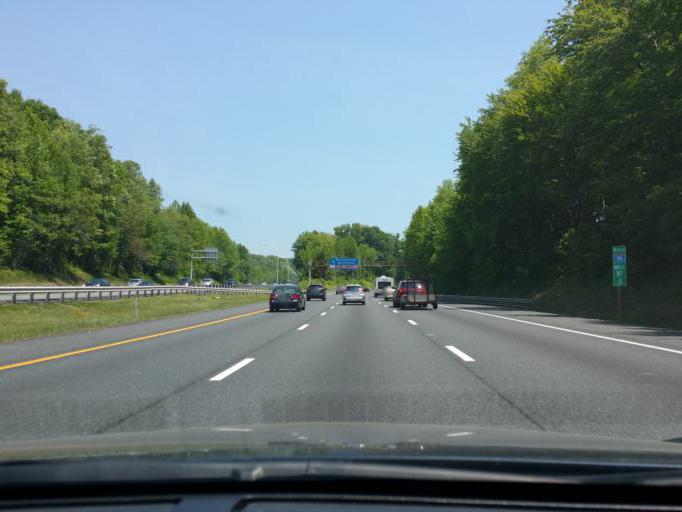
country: US
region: Maryland
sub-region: Harford County
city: Riverside
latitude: 39.4907
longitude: -76.2398
